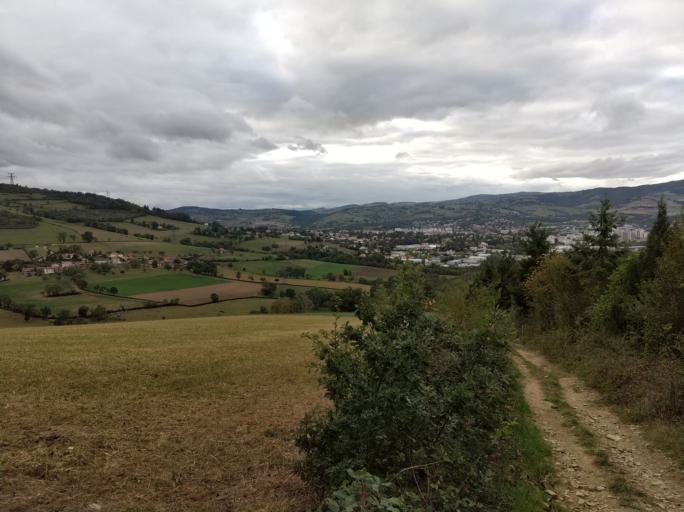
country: FR
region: Rhone-Alpes
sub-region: Departement de la Loire
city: Saint-Paul-en-Jarez
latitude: 45.4609
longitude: 4.5520
